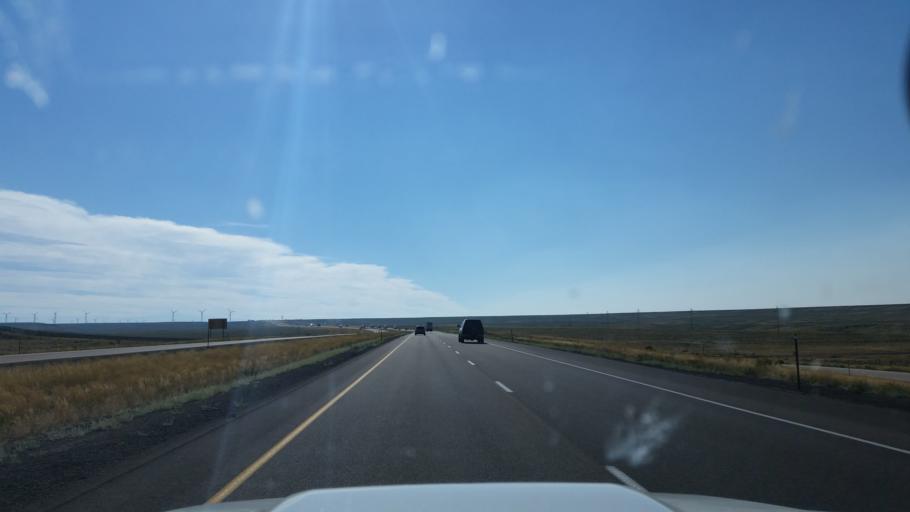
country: US
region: Wyoming
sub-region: Uinta County
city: Mountain View
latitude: 41.3281
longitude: -110.4562
